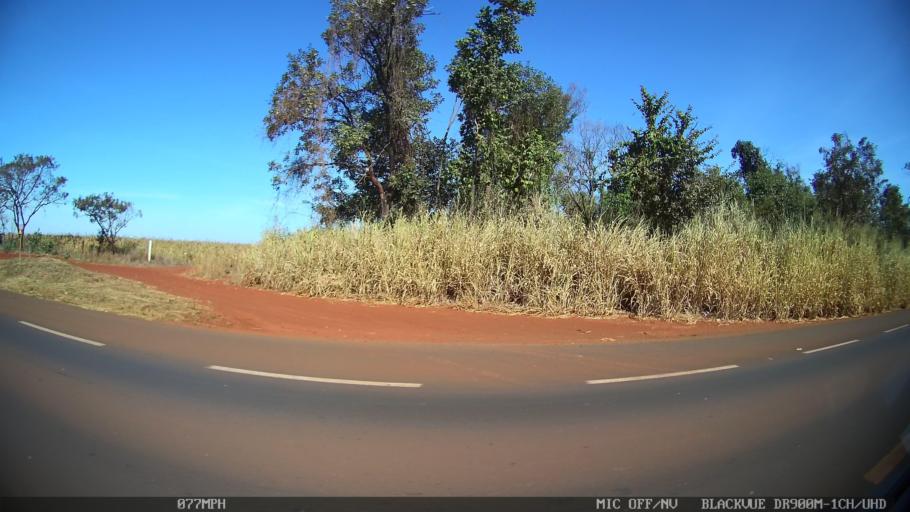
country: BR
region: Sao Paulo
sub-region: Guaira
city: Guaira
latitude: -20.4448
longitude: -48.3798
